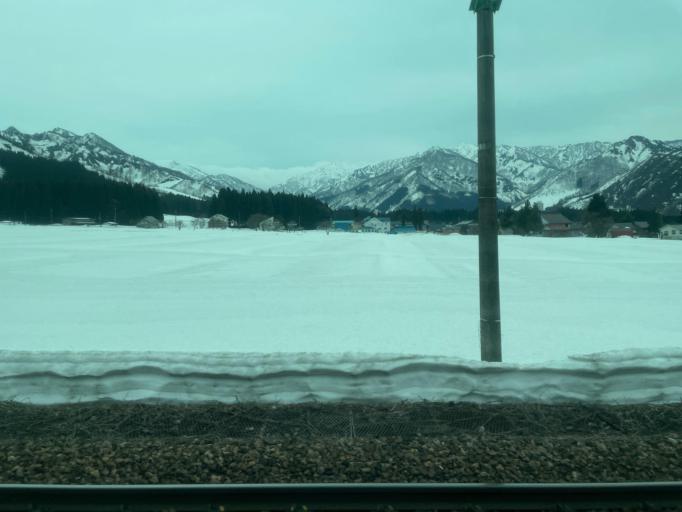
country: JP
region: Niigata
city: Shiozawa
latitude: 36.9301
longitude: 138.8483
